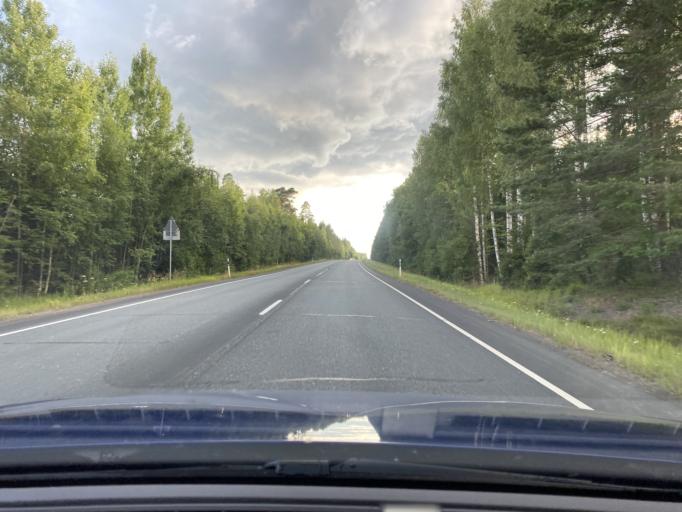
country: FI
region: Haeme
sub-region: Haemeenlinna
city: Renko
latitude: 60.8490
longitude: 24.1446
